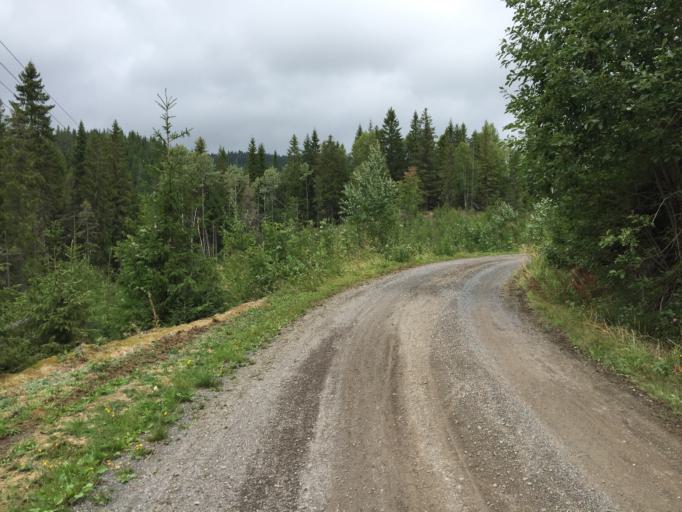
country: NO
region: Akershus
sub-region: Baerum
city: Sandvika
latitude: 60.0201
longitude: 10.5515
